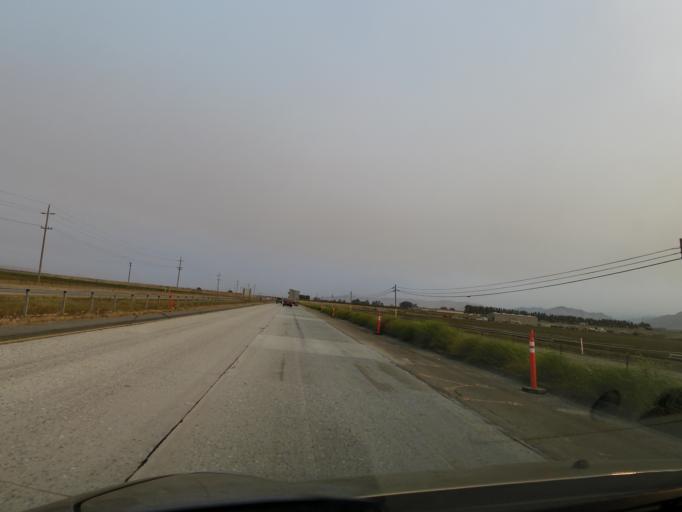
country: US
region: California
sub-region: Monterey County
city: Soledad
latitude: 36.3931
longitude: -121.3096
